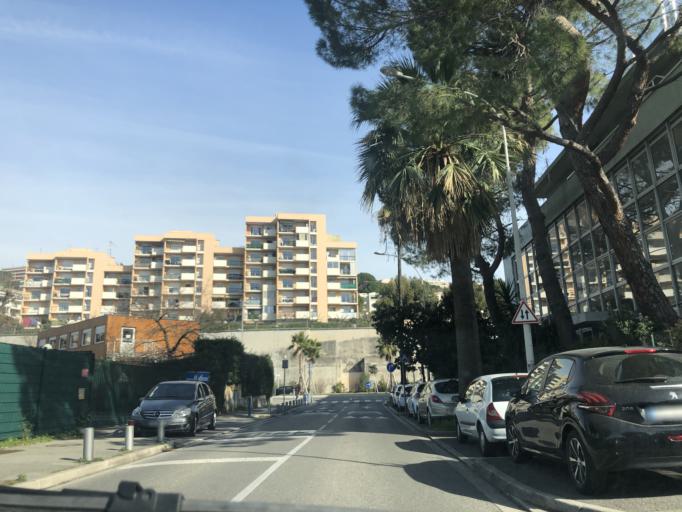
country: FR
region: Provence-Alpes-Cote d'Azur
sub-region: Departement des Alpes-Maritimes
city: Saint-Laurent-du-Var
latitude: 43.6859
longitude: 7.2010
